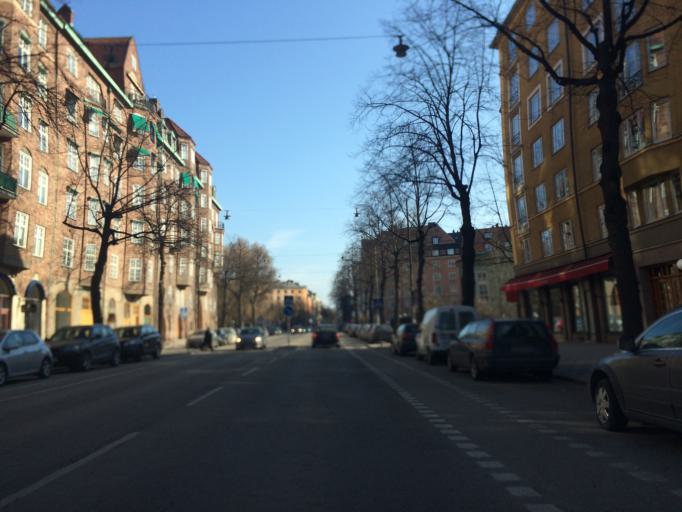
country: SE
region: Stockholm
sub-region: Stockholms Kommun
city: Stockholm
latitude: 59.3446
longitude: 18.0644
